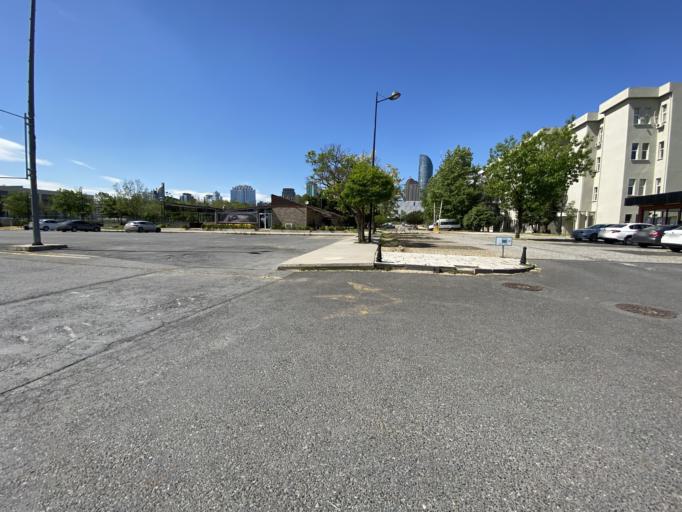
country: TR
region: Istanbul
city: Sisli
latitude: 41.1030
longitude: 29.0241
